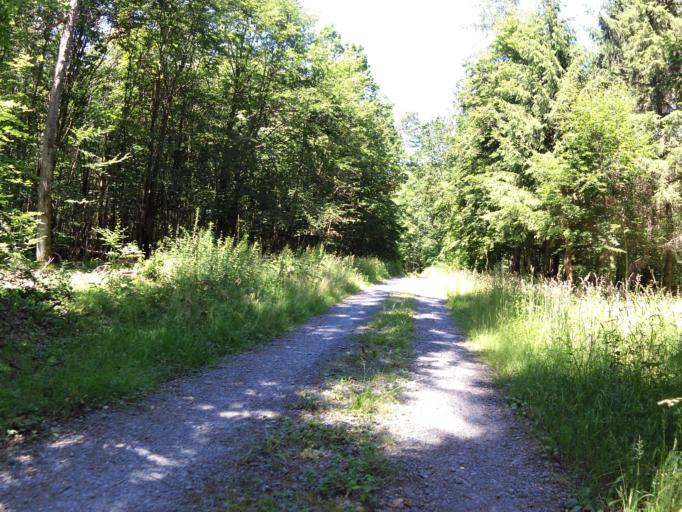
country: DE
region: Bavaria
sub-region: Regierungsbezirk Unterfranken
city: Wuerzburg
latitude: 49.7242
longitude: 9.8774
